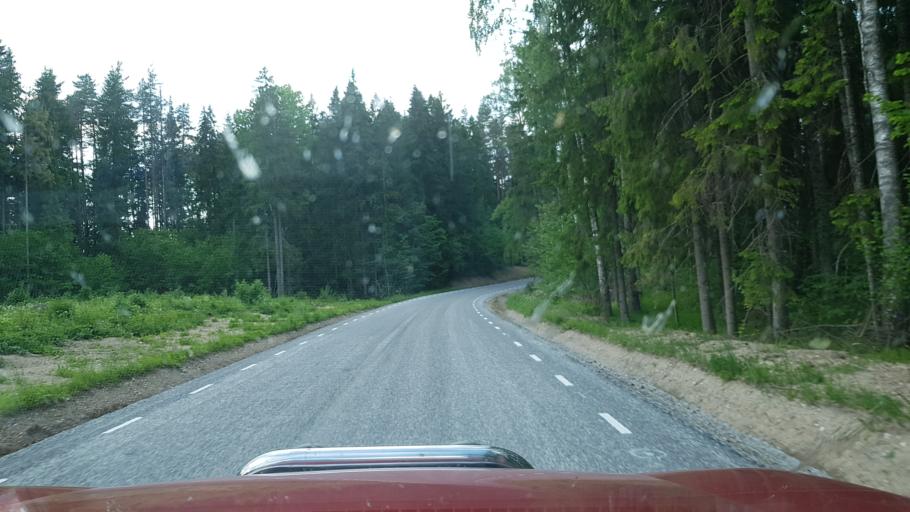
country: EE
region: Tartu
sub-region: UElenurme vald
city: Ulenurme
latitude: 58.0941
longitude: 26.8062
